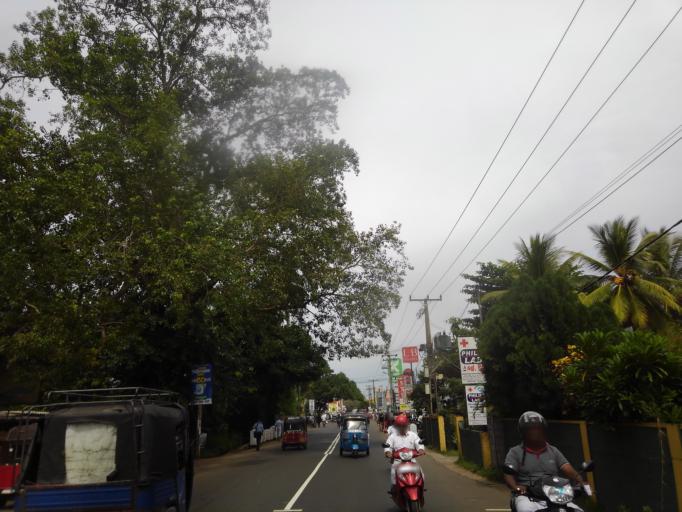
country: LK
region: Western
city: Beruwala
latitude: 6.4735
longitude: 79.9842
